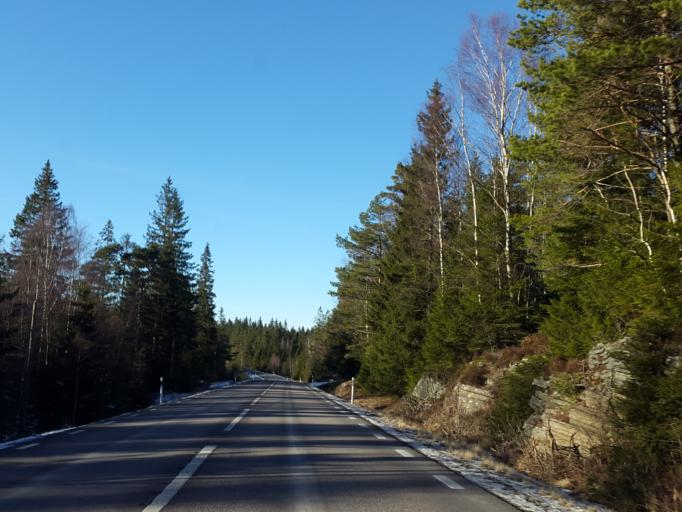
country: SE
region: Vaestra Goetaland
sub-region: Boras Kommun
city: Sandared
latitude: 57.8254
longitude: 12.7219
